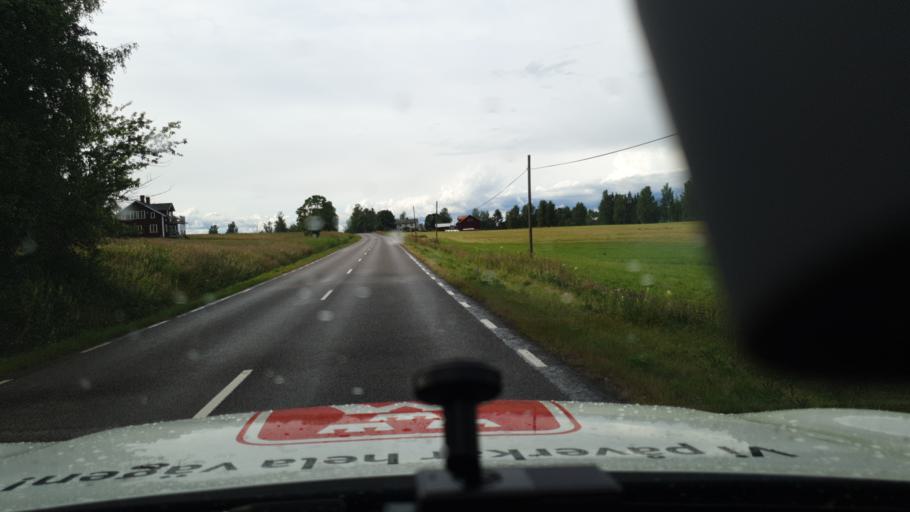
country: SE
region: Vaermland
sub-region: Sunne Kommun
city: Sunne
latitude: 59.8088
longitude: 13.0320
